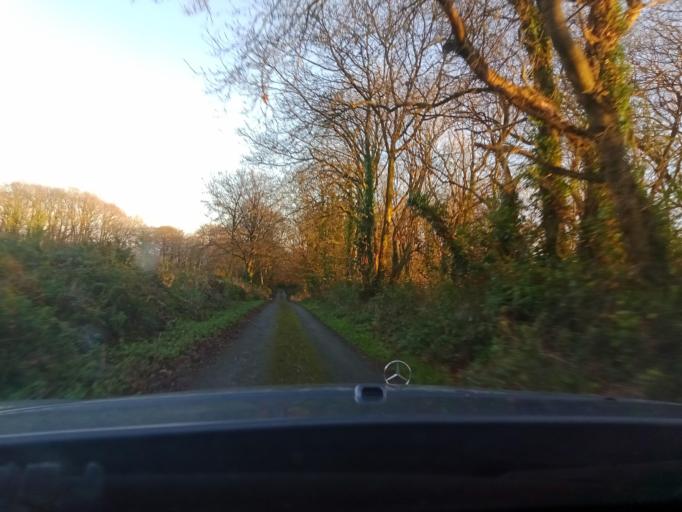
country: IE
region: Leinster
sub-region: Kilkenny
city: Graiguenamanagh
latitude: 52.4696
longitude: -6.9538
